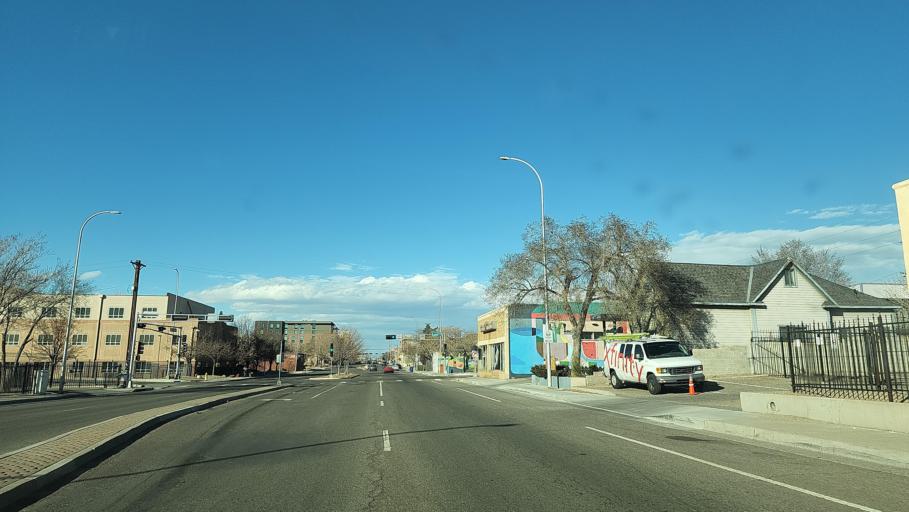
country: US
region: New Mexico
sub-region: Bernalillo County
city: Albuquerque
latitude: 35.0801
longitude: -106.6453
